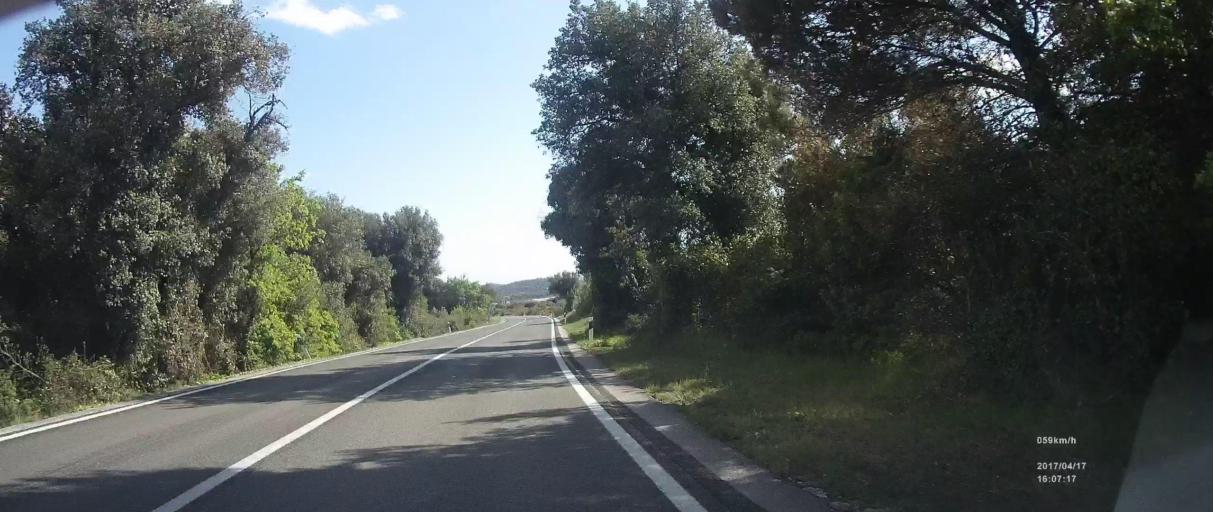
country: HR
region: Sibensko-Kniniska
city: Rogoznica
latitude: 43.5510
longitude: 15.9607
